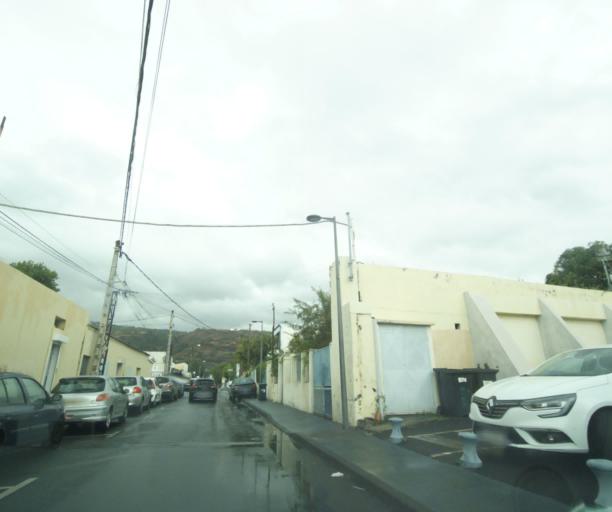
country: RE
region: Reunion
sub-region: Reunion
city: Saint-Paul
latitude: -21.0096
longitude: 55.2694
